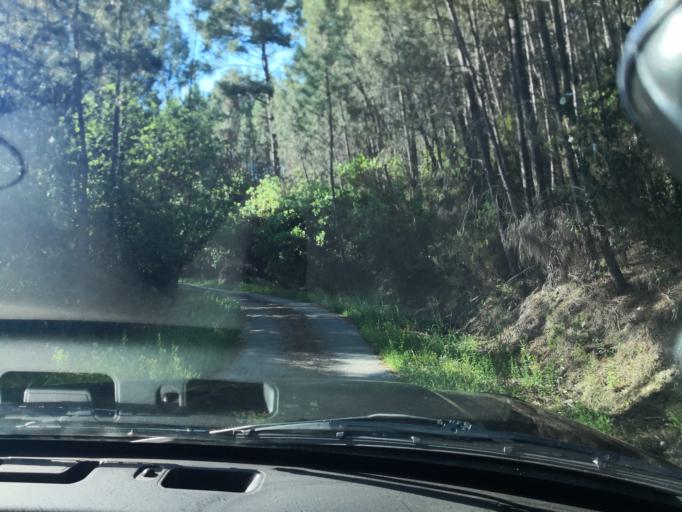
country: PT
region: Vila Real
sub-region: Vila Real
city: Vila Real
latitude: 41.2744
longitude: -7.7480
